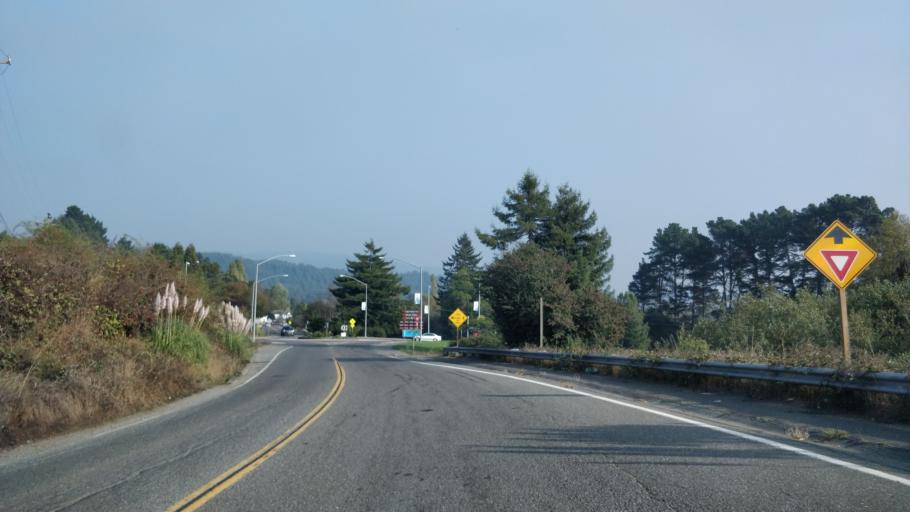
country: US
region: California
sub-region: Humboldt County
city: Blue Lake
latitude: 40.8867
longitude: -123.9966
